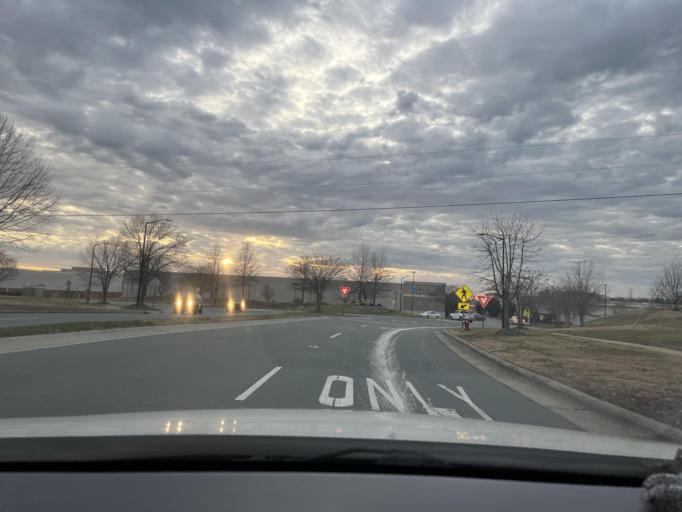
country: US
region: North Carolina
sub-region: Alamance County
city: Elon
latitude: 36.0709
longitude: -79.5043
